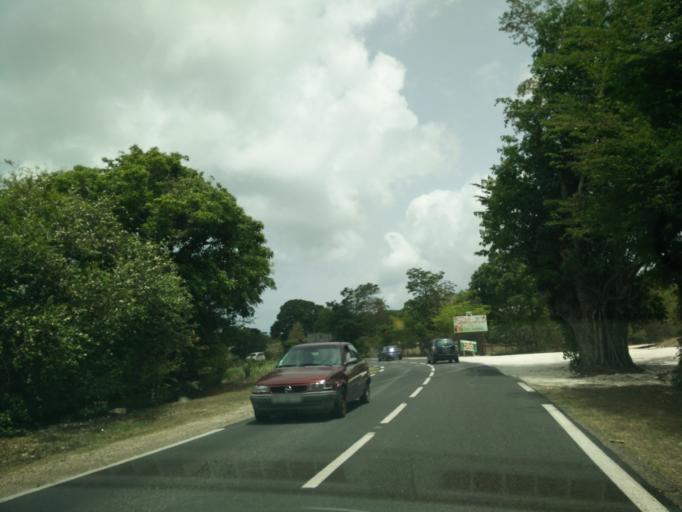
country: GP
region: Guadeloupe
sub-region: Guadeloupe
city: Petit-Canal
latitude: 16.3773
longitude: -61.4785
